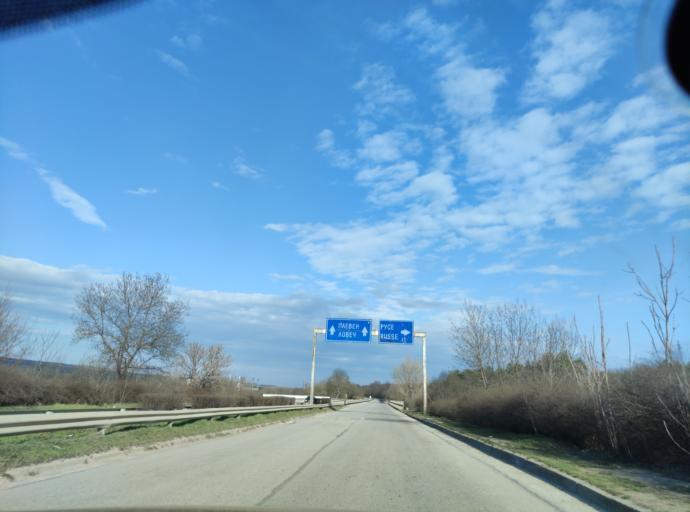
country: BG
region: Pleven
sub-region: Obshtina Dolna Mitropoliya
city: Dolna Mitropoliya
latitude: 43.4330
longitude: 24.5481
